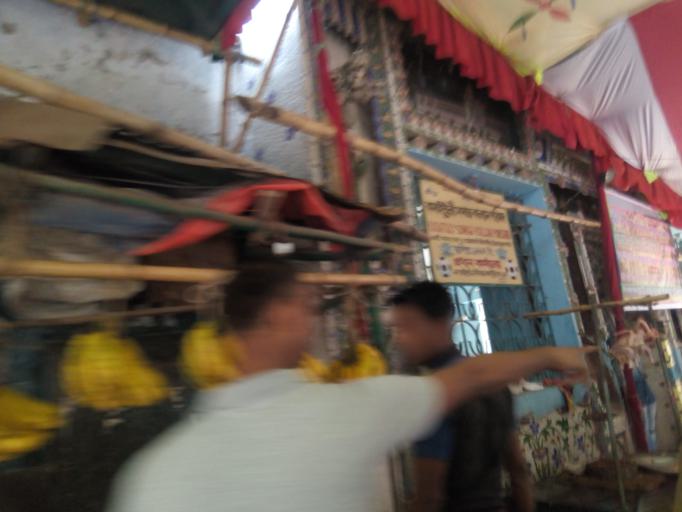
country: BD
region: Dhaka
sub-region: Dhaka
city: Dhaka
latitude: 23.7156
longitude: 90.4042
